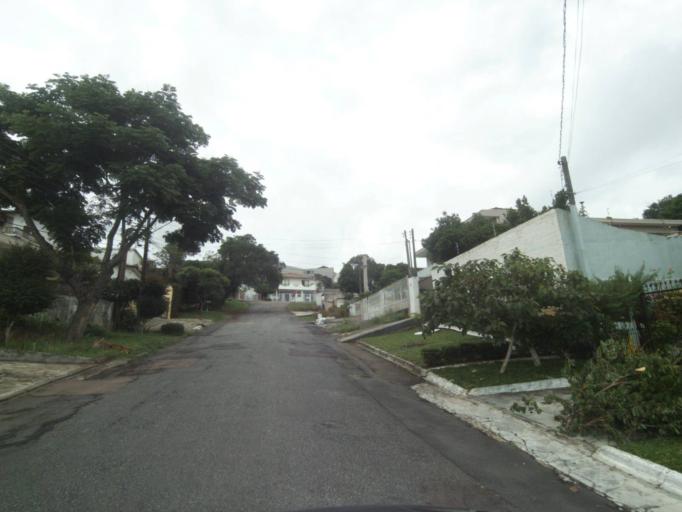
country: BR
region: Parana
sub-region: Curitiba
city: Curitiba
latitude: -25.4740
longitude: -49.3303
